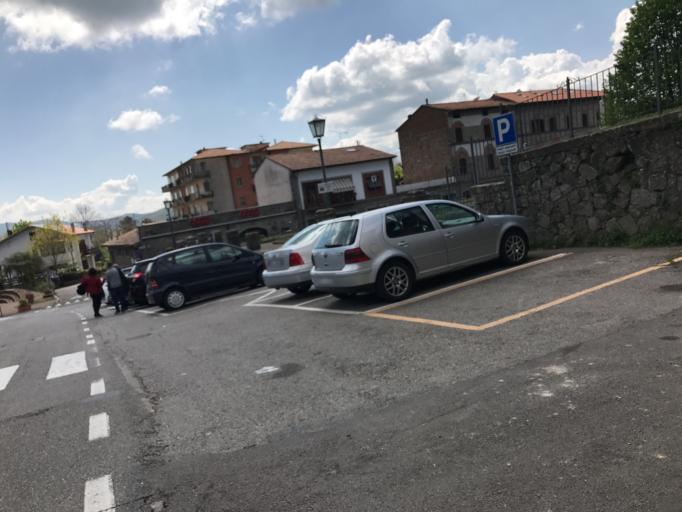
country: IT
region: Tuscany
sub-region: Provincia di Grosseto
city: Santa Fiora
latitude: 42.8333
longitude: 11.5877
